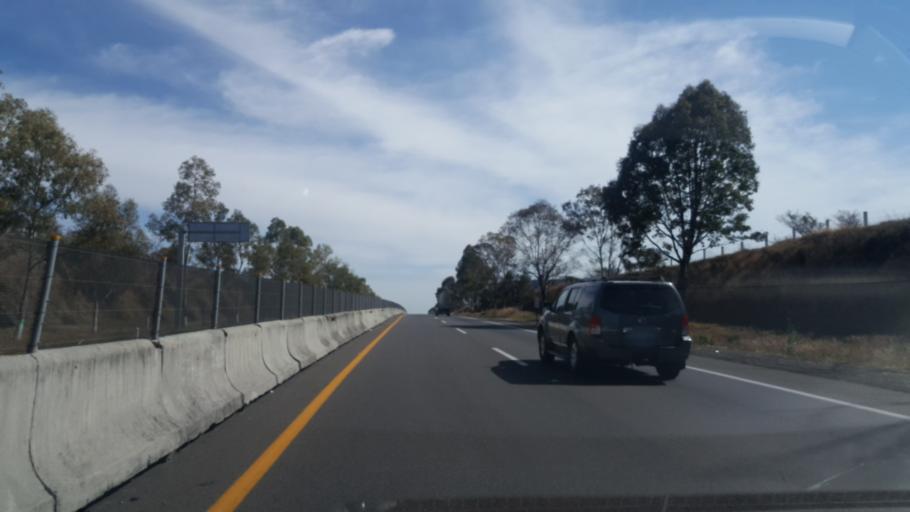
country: MX
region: Jalisco
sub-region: Lagos de Moreno
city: Cristeros [Fraccionamiento]
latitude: 21.3084
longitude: -102.0290
